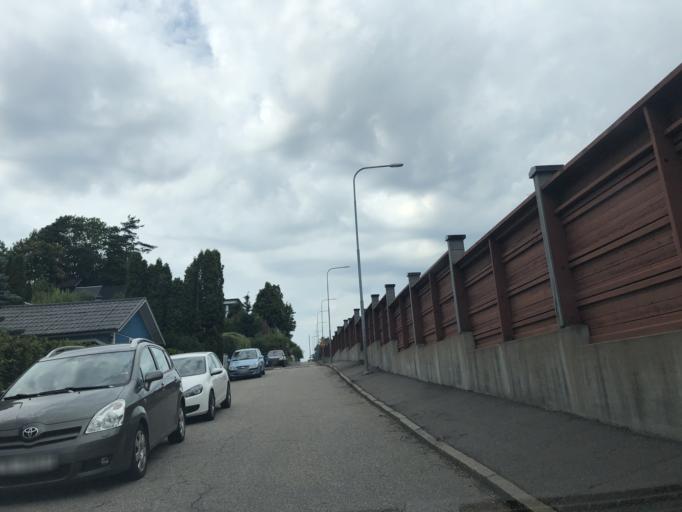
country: SE
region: Vaestra Goetaland
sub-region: Goteborg
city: Majorna
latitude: 57.7368
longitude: 11.9098
